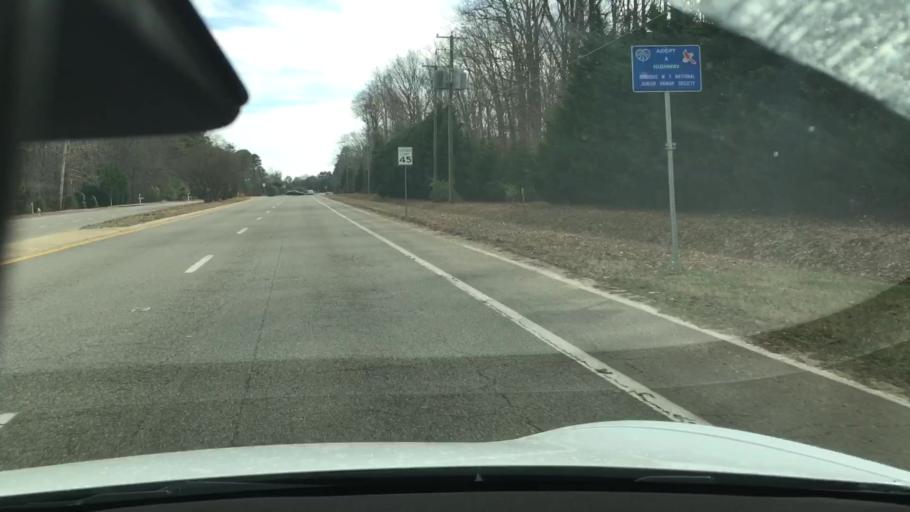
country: US
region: Virginia
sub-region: Chesterfield County
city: Bon Air
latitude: 37.5336
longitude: -77.6332
